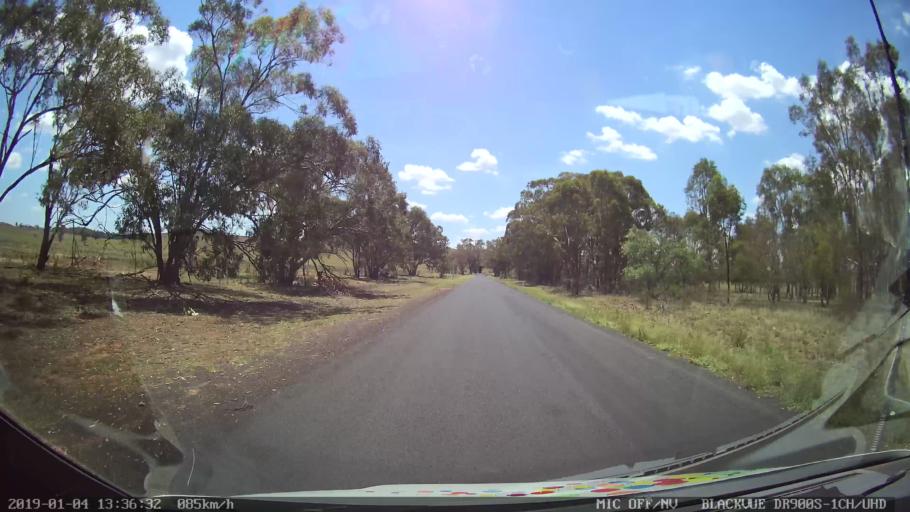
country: AU
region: New South Wales
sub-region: Dubbo Municipality
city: Dubbo
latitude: -32.5595
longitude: 148.5377
